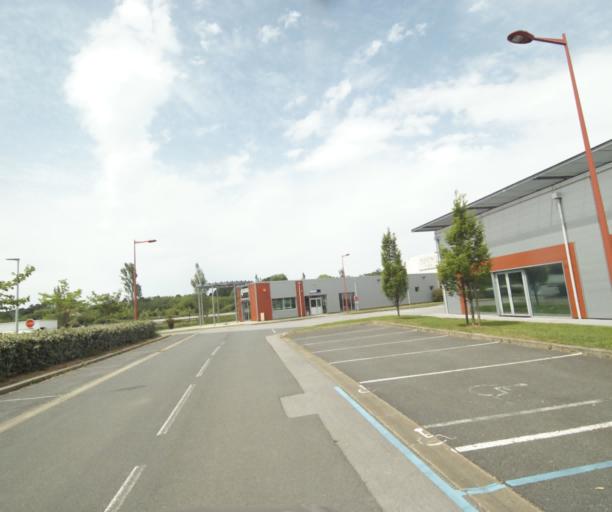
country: FR
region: Aquitaine
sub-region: Departement des Pyrenees-Atlantiques
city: Mouguerre
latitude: 43.4893
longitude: -1.4314
